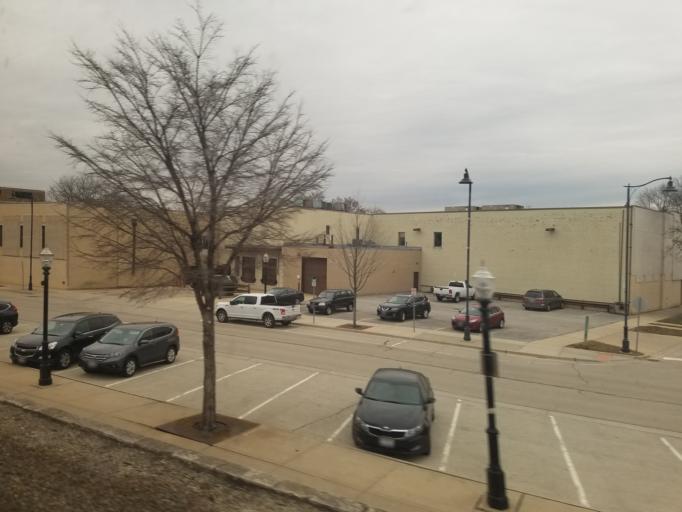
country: US
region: Illinois
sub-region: Cook County
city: La Grange
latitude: 41.8154
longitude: -87.8736
